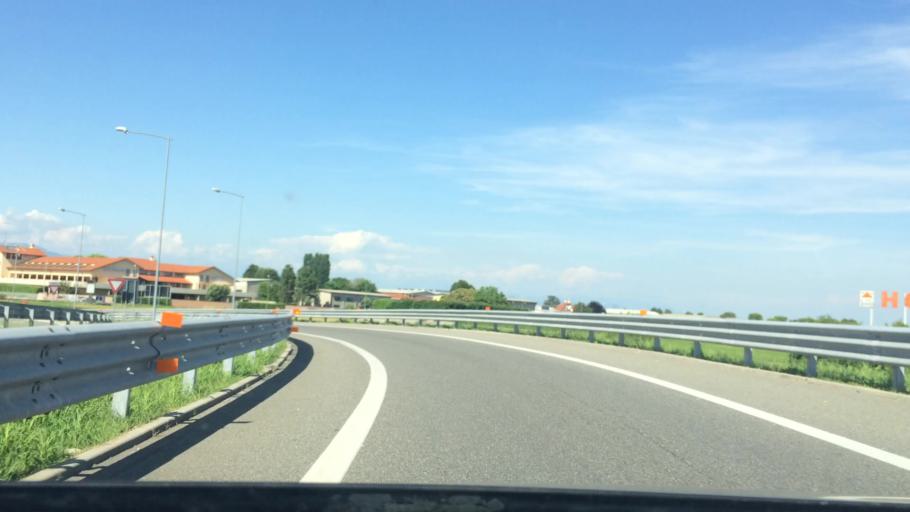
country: IT
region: Lombardy
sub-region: Provincia di Como
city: Turate
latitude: 45.6526
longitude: 9.0167
